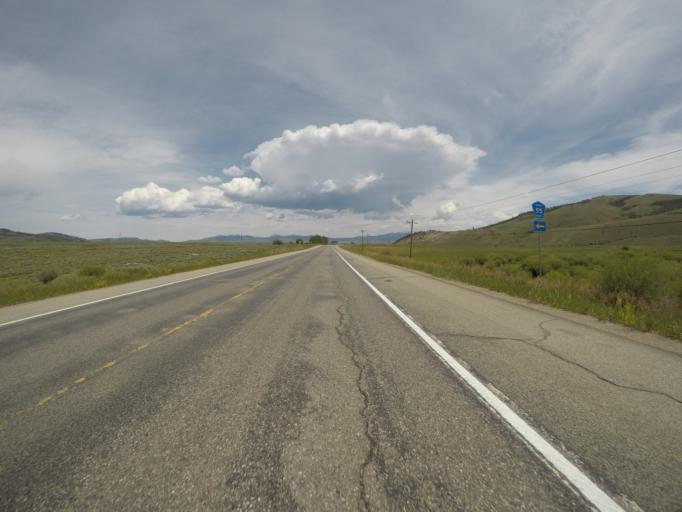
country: US
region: Colorado
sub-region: Grand County
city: Granby
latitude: 40.0290
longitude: -105.9404
